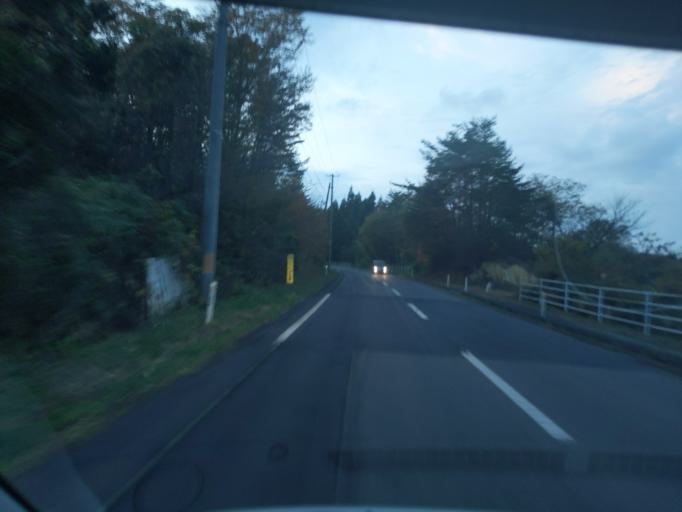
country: JP
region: Iwate
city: Ichinoseki
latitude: 38.9358
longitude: 141.0514
